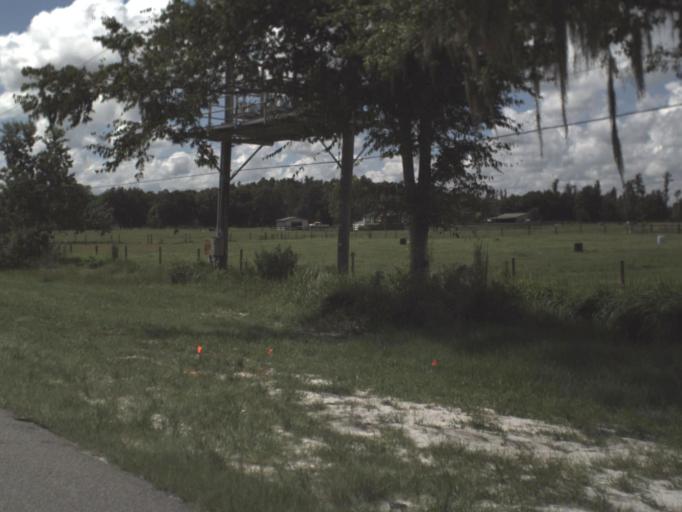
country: US
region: Florida
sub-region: Polk County
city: Polk City
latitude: 28.2578
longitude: -81.8244
